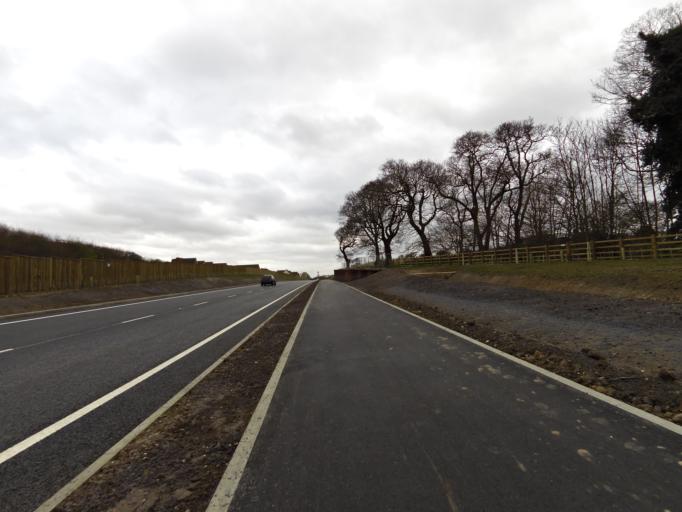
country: GB
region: England
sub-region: Norfolk
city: Hopton on Sea
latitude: 52.5031
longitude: 1.7283
